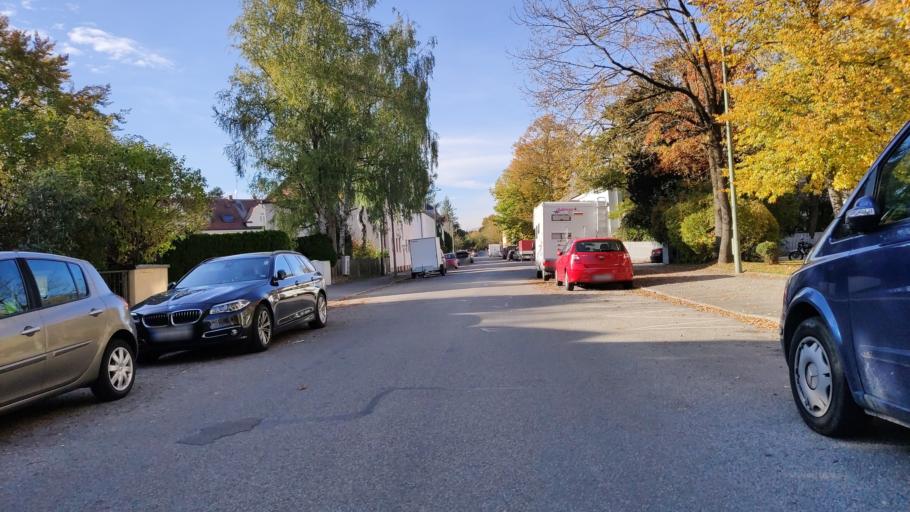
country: DE
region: Bavaria
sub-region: Upper Bavaria
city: Pasing
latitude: 48.1413
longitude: 11.4663
